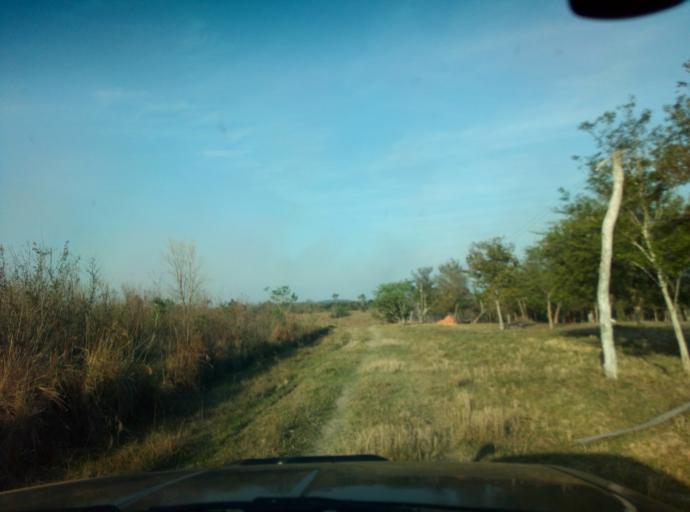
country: PY
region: Caaguazu
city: Doctor Cecilio Baez
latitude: -25.1999
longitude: -56.1222
